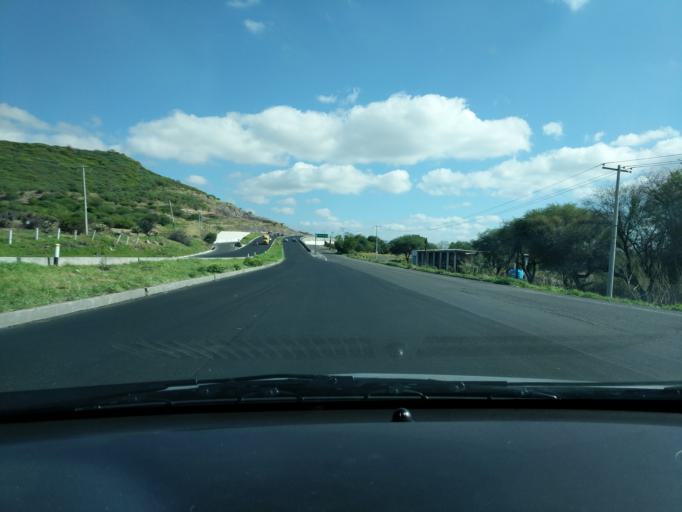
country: MX
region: Guanajuato
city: El Castillo
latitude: 20.6011
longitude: -100.4907
